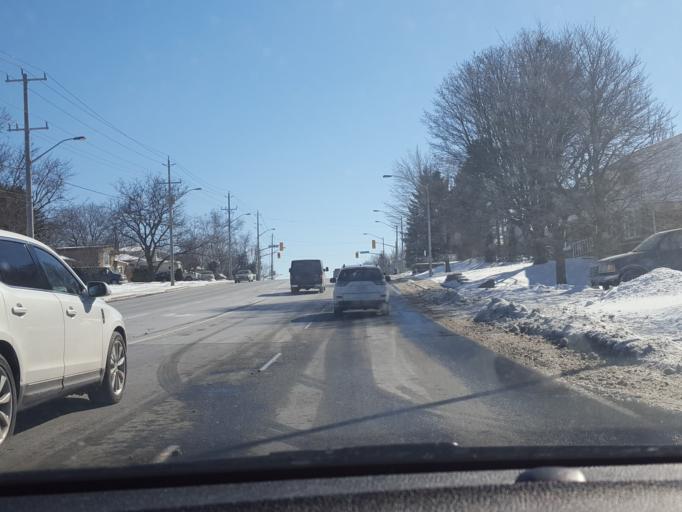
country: CA
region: Ontario
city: Kitchener
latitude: 43.4248
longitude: -80.5204
